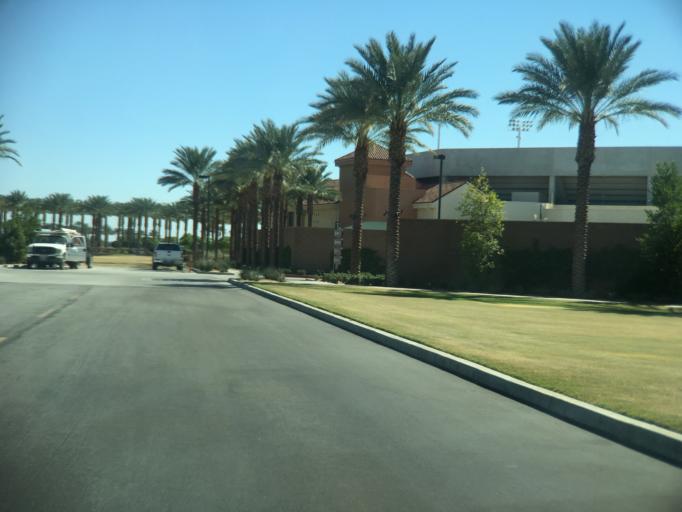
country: US
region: California
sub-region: Riverside County
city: Bermuda Dunes
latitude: 33.7262
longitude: -116.3037
